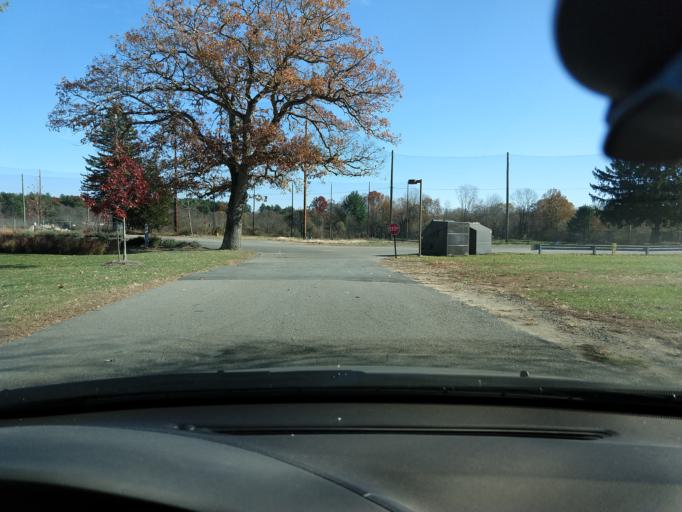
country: US
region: Massachusetts
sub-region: Middlesex County
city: Bedford
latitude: 42.5050
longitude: -71.2706
